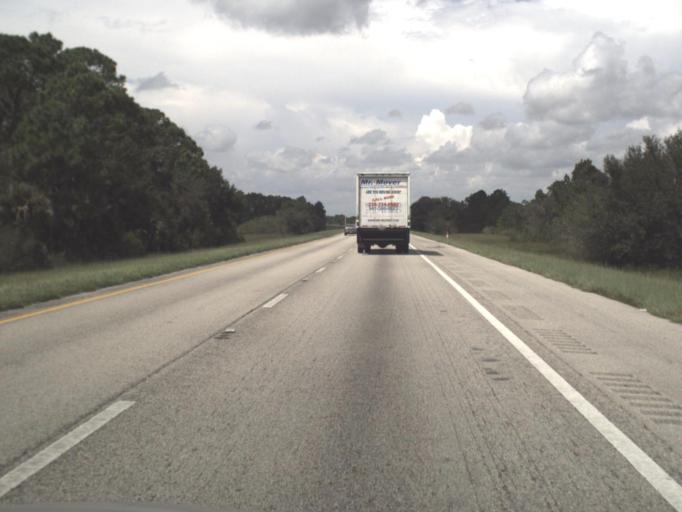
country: US
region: Florida
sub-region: Lee County
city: Suncoast Estates
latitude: 26.7914
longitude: -81.9047
